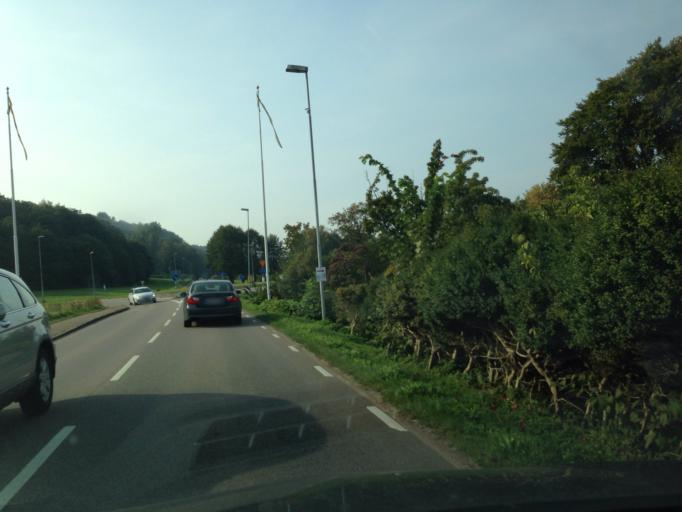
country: SE
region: Skane
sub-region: Bastads Kommun
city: Bastad
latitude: 56.4343
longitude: 12.8296
